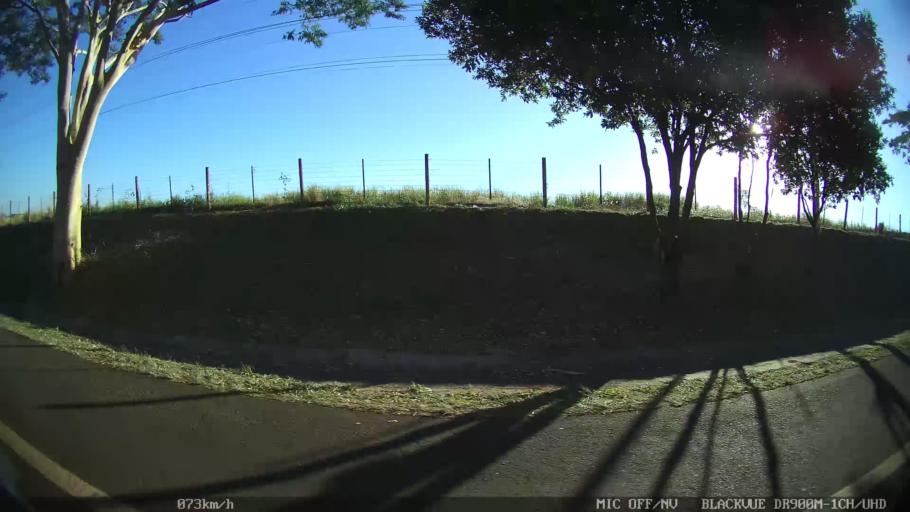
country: BR
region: Sao Paulo
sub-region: Guapiacu
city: Guapiacu
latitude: -20.7807
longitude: -49.2243
